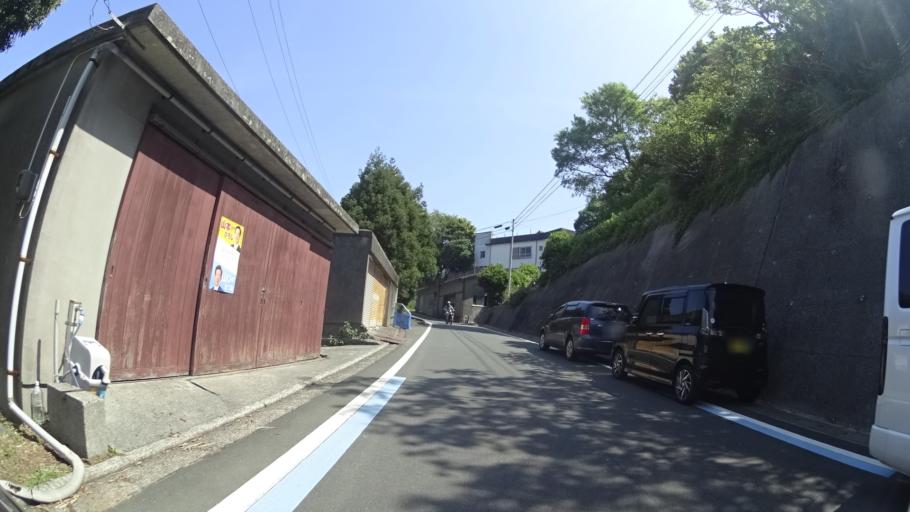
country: JP
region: Ehime
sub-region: Nishiuwa-gun
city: Ikata-cho
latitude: 33.3686
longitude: 132.0492
